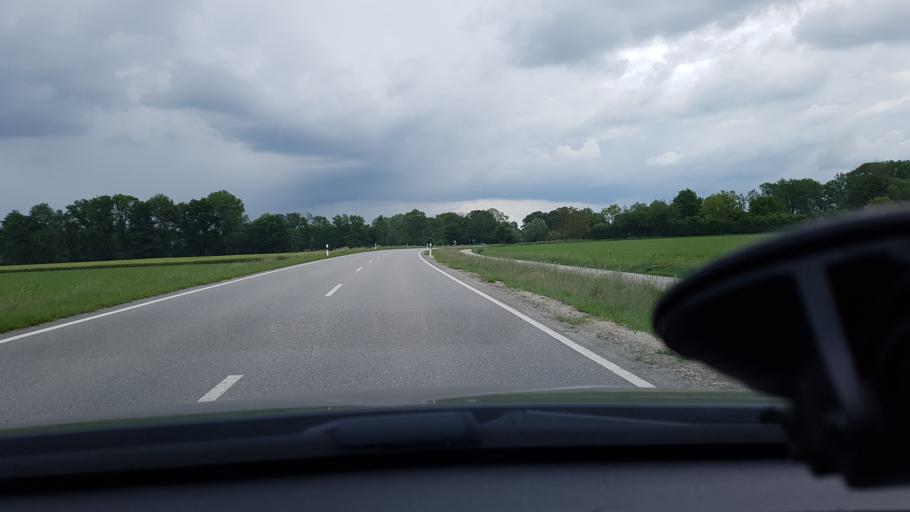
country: DE
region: Bavaria
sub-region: Lower Bavaria
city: Pocking
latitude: 48.4072
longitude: 13.3679
